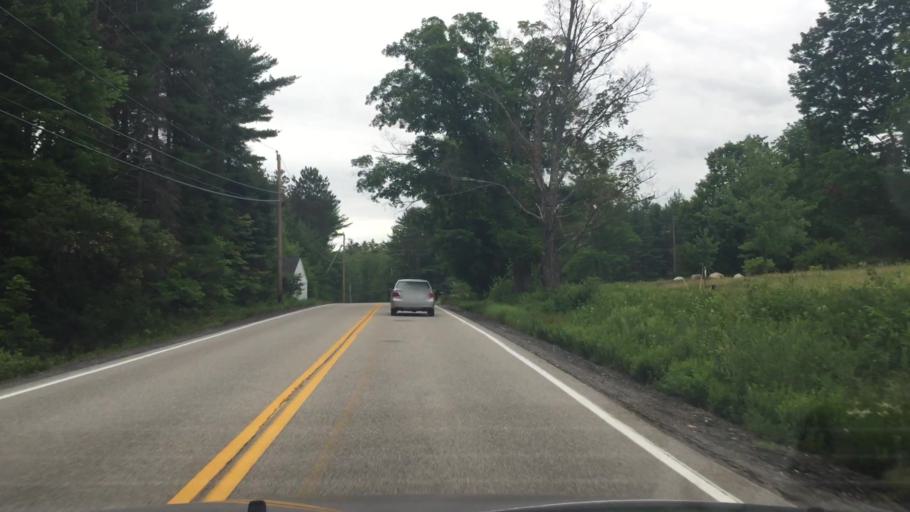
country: US
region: New Hampshire
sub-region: Carroll County
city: Conway
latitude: 43.9675
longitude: -71.1098
